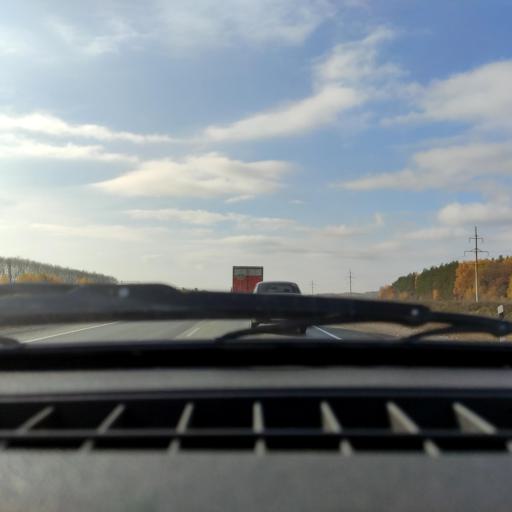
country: RU
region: Bashkortostan
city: Kabakovo
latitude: 54.7160
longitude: 56.2325
